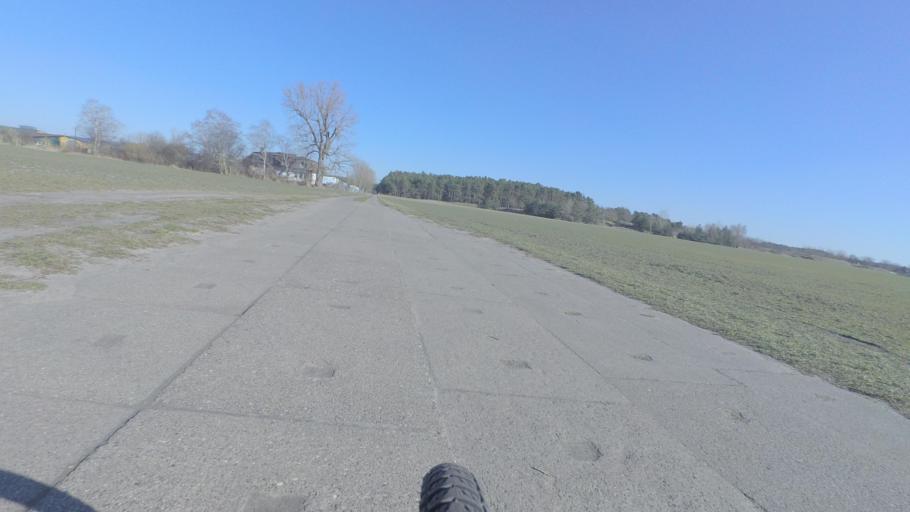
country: DE
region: Brandenburg
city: Rangsdorf
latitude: 52.2548
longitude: 13.4135
